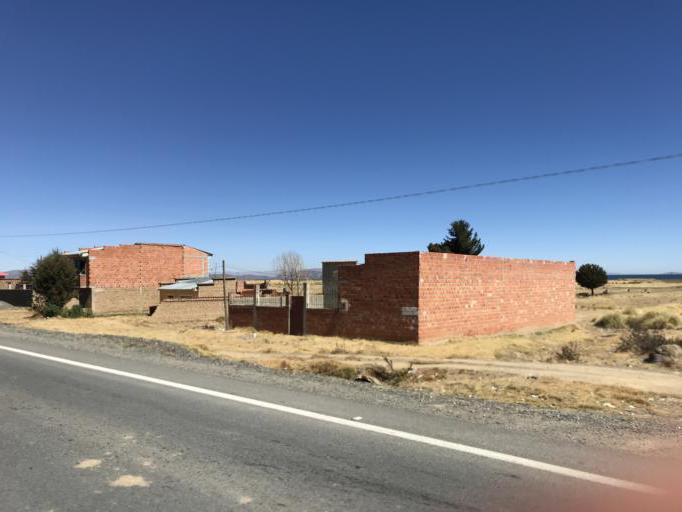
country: BO
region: La Paz
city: Huarina
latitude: -16.2047
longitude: -68.5957
